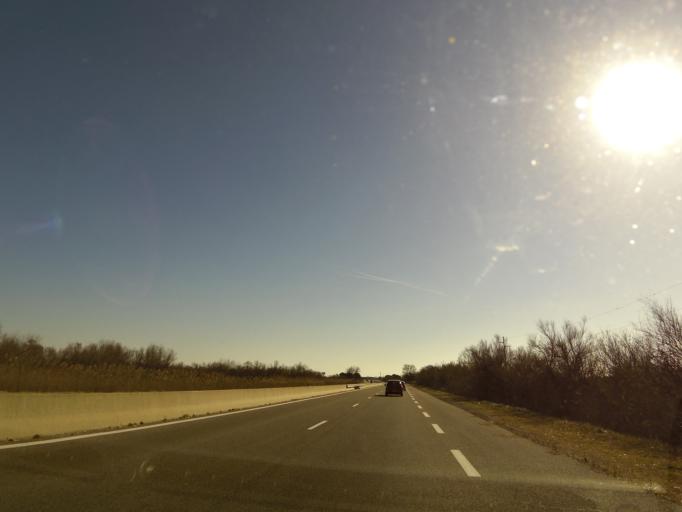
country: FR
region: Languedoc-Roussillon
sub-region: Departement du Gard
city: Aigues-Mortes
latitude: 43.6028
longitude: 4.1946
